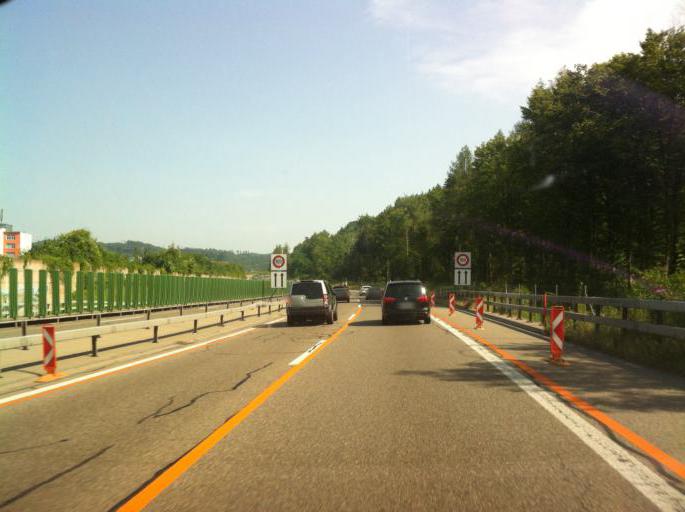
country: CH
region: Zurich
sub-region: Bezirk Winterthur
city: Wuelflingen (Kreis 6) / Oberfeld
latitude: 47.4970
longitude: 8.6946
